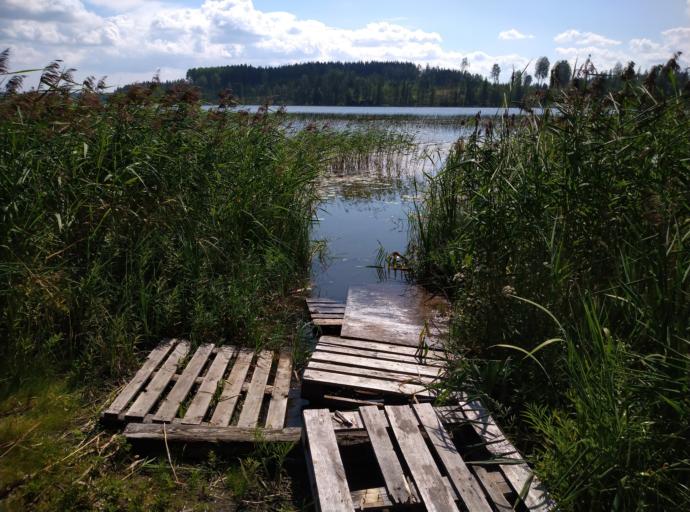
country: FI
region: South Karelia
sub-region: Lappeenranta
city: Lappeenranta
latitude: 61.0335
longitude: 28.3435
